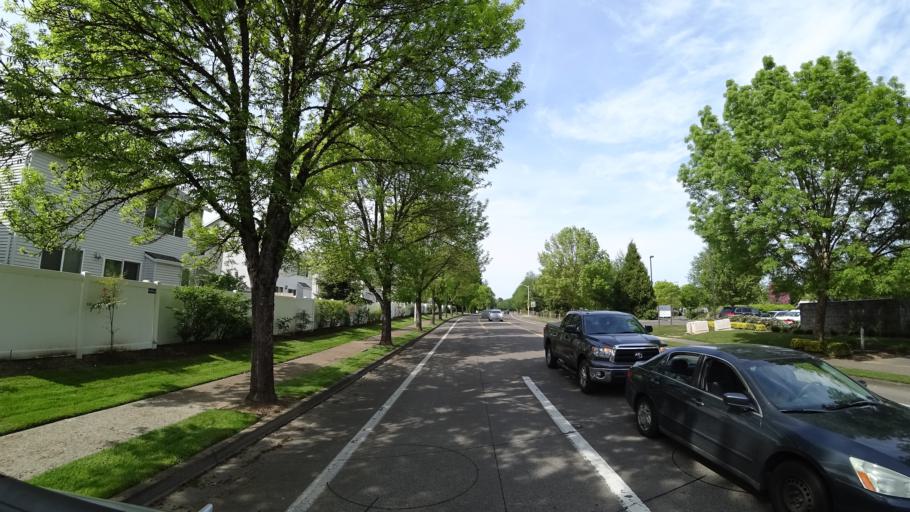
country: US
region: Oregon
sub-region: Washington County
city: Rockcreek
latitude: 45.5202
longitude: -122.9291
